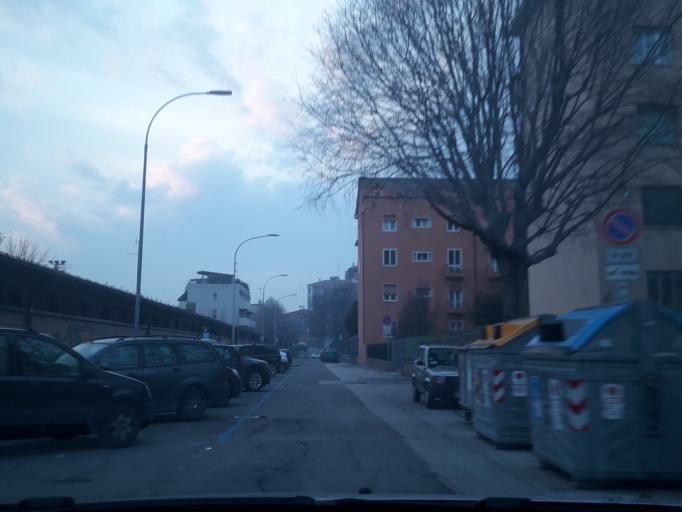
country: IT
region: Emilia-Romagna
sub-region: Provincia di Bologna
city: Bologna
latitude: 44.5002
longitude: 11.3099
